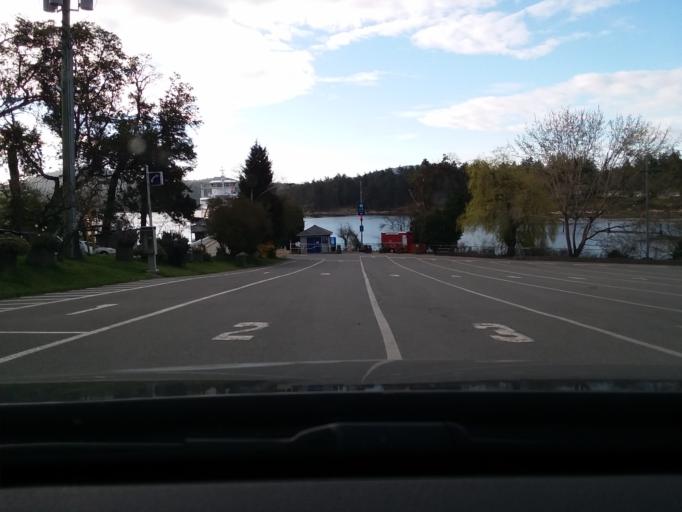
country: CA
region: British Columbia
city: North Saanich
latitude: 48.8785
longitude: -123.3173
